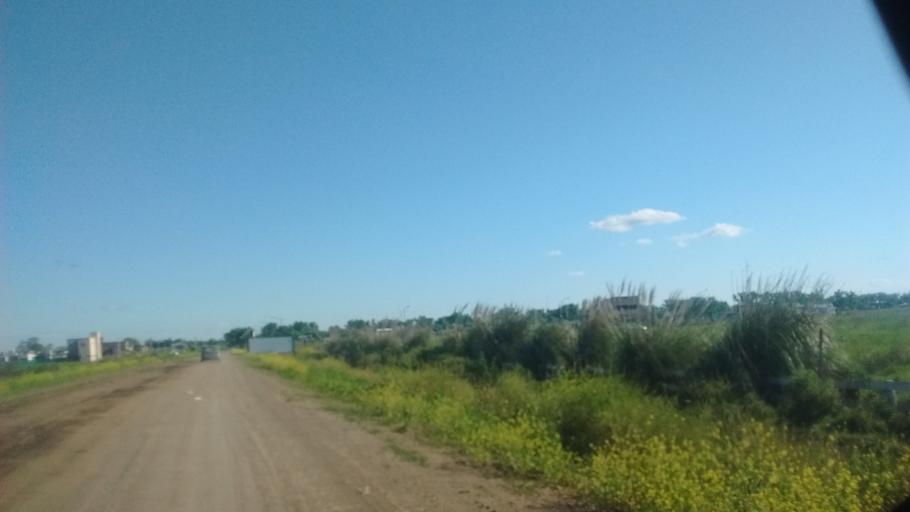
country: AR
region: Santa Fe
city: Funes
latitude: -32.8974
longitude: -60.8051
